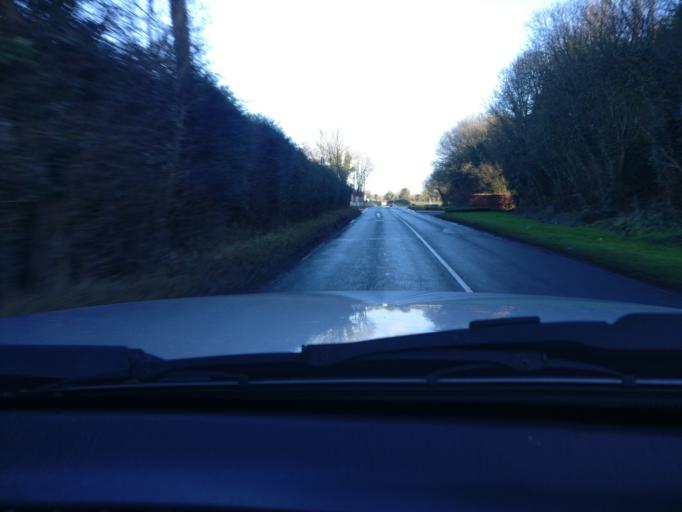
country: IE
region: Leinster
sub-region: An Iarmhi
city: An Muileann gCearr
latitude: 53.5153
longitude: -7.3841
